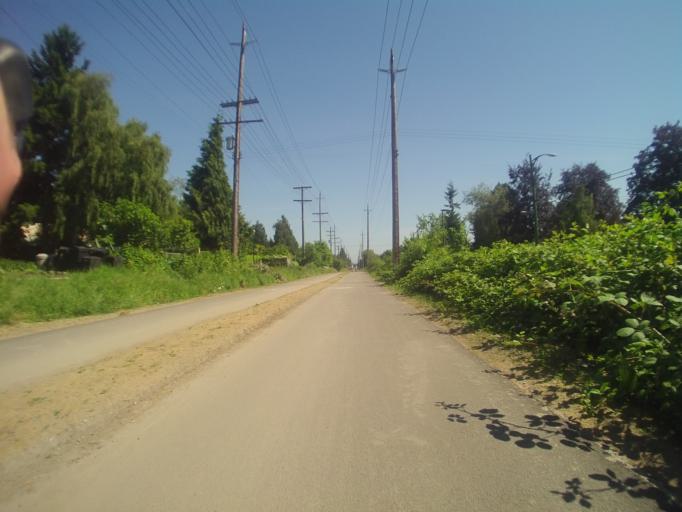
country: CA
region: British Columbia
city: Vancouver
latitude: 49.2248
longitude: -123.1535
